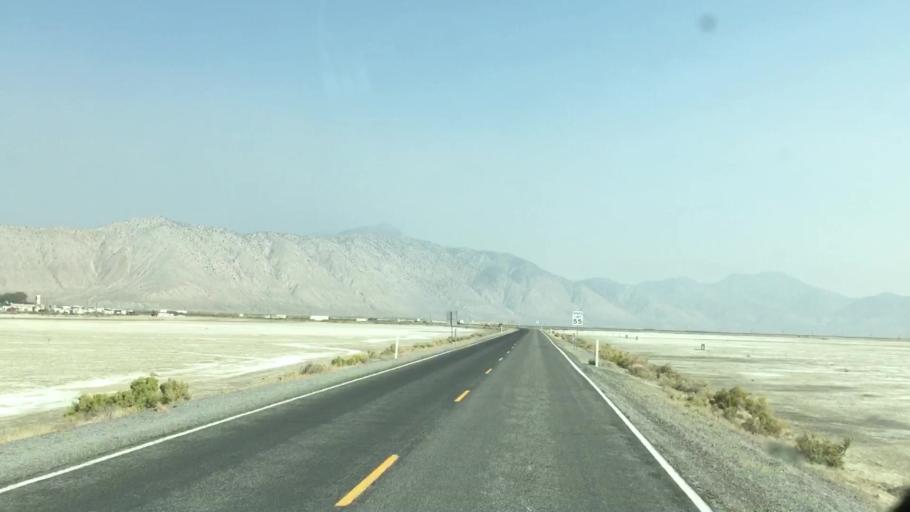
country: US
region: Nevada
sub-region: Pershing County
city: Lovelock
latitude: 40.6475
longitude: -119.3432
